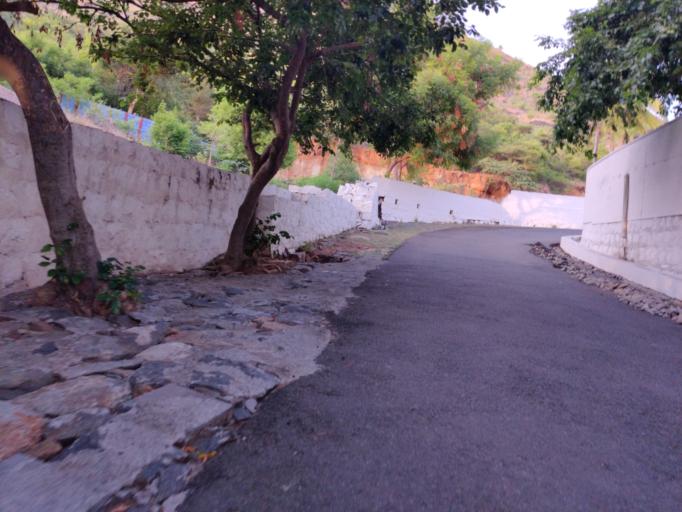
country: IN
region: Tamil Nadu
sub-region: Salem
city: Salem
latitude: 11.6201
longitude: 78.1513
